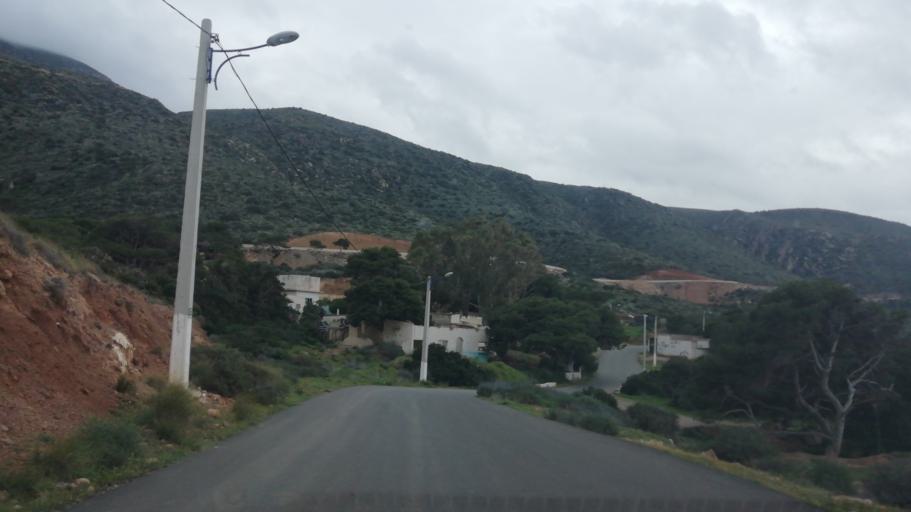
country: DZ
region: Oran
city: Bir el Djir
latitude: 35.7766
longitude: -0.5148
